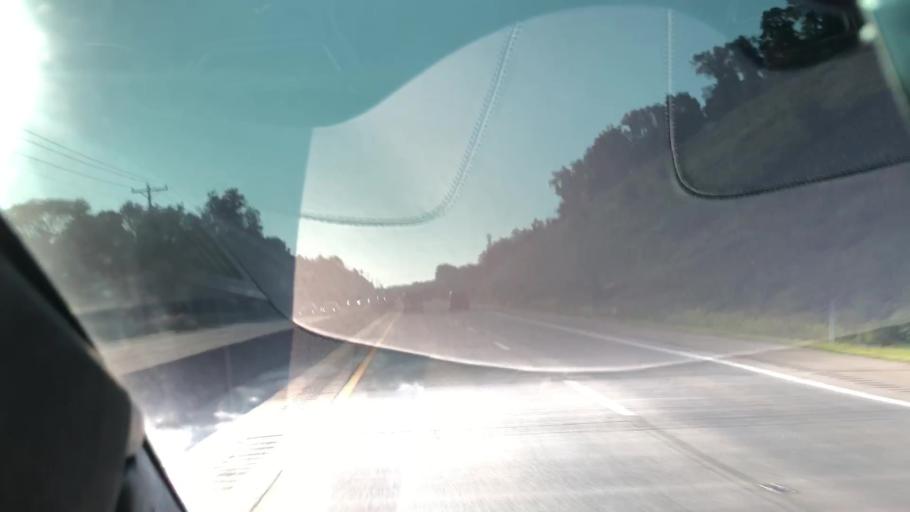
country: US
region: Pennsylvania
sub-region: Westmoreland County
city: Murrysville
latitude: 40.4172
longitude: -79.6479
